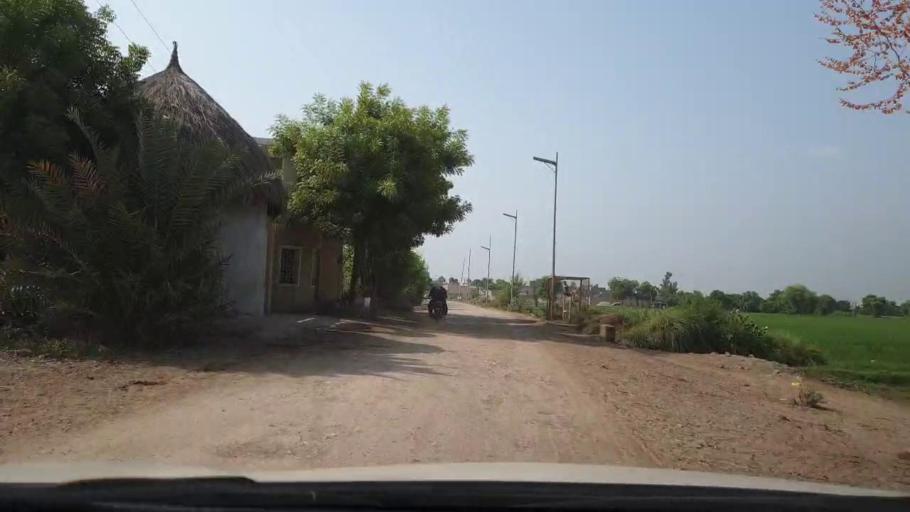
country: PK
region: Sindh
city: Larkana
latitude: 27.4627
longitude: 68.2297
